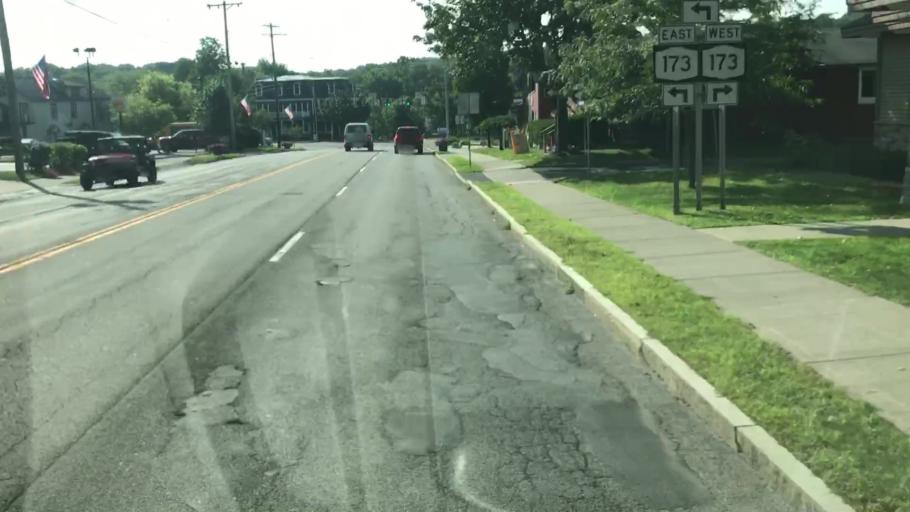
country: US
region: New York
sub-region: Onondaga County
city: Manlius
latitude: 43.0021
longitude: -75.9803
